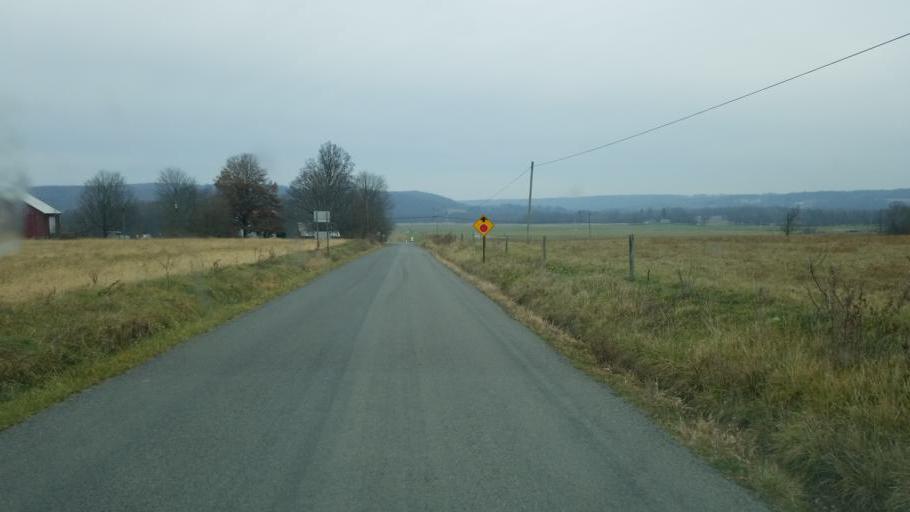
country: US
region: Pennsylvania
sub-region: Crawford County
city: Cochranton
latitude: 41.5246
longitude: -80.1247
